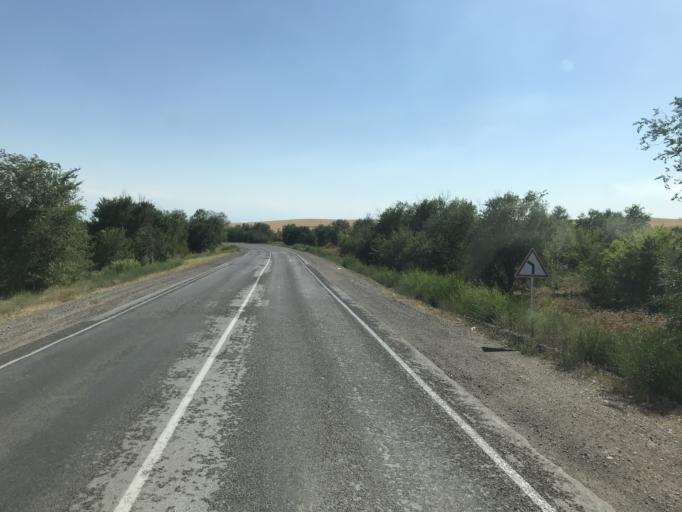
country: KZ
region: Zhambyl
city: Georgiyevka
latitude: 43.1582
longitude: 74.7077
